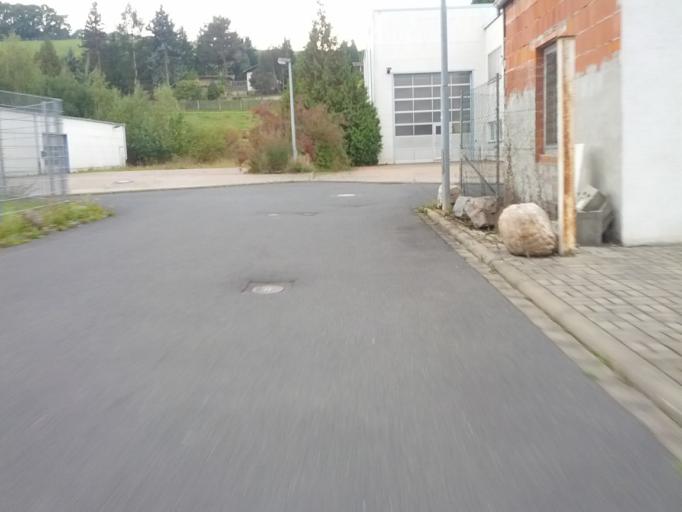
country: DE
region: Thuringia
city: Thal
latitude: 50.9475
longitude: 10.3906
